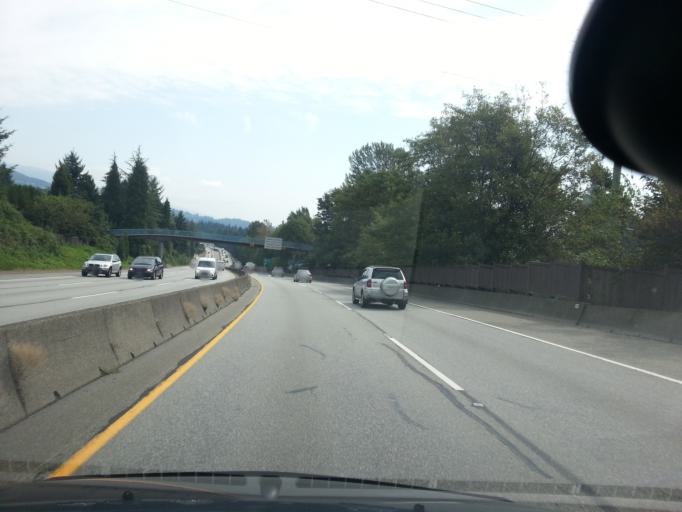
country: CA
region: British Columbia
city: West Vancouver
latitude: 49.3386
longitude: -123.1461
